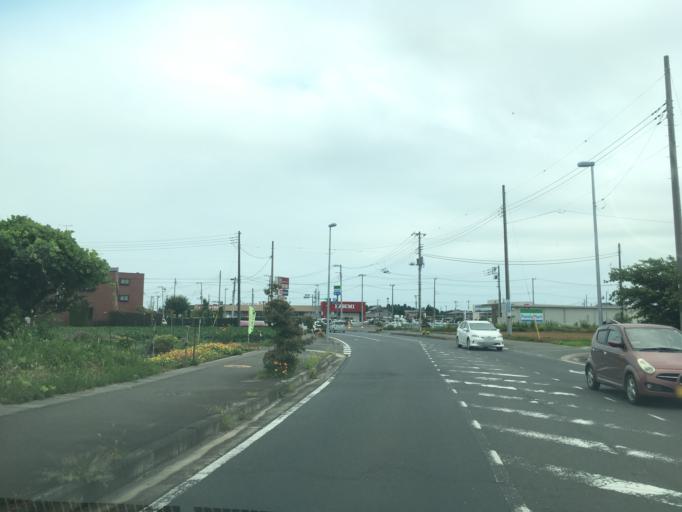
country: JP
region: Ibaraki
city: Hitachi-Naka
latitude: 36.4081
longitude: 140.5641
